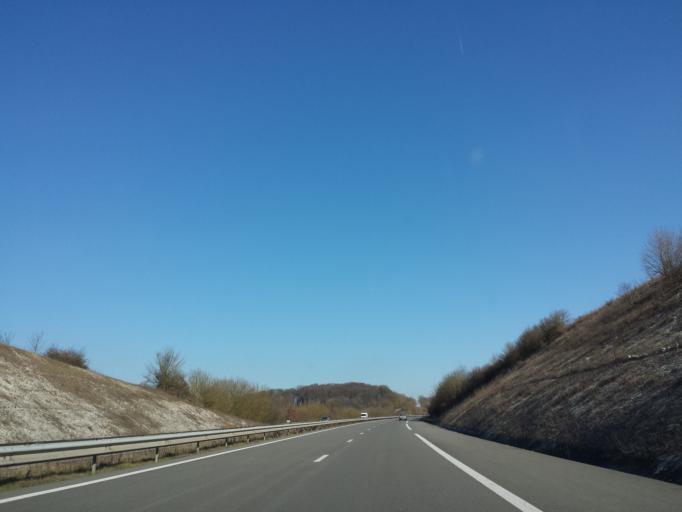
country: FR
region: Picardie
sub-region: Departement de la Somme
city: Conty
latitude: 49.6756
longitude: 2.2112
